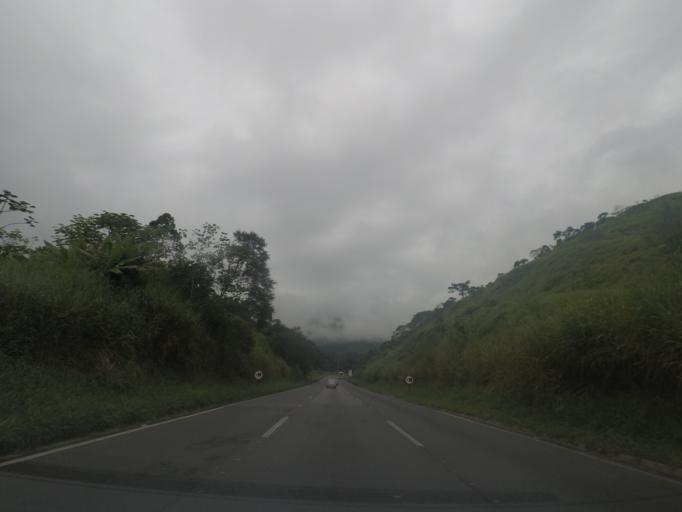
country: BR
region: Sao Paulo
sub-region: Cajati
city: Cajati
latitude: -24.8696
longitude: -48.2162
